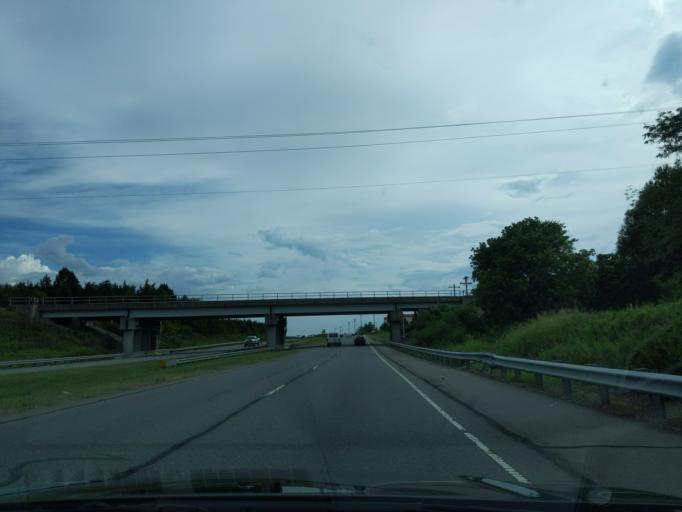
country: US
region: North Carolina
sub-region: Cabarrus County
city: Harrisburg
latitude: 35.3510
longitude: -80.6056
